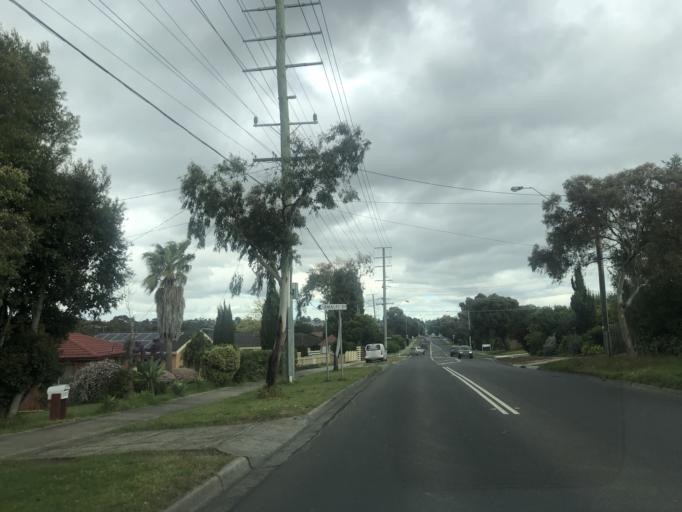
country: AU
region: Victoria
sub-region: Casey
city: Endeavour Hills
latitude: -37.9743
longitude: 145.2421
